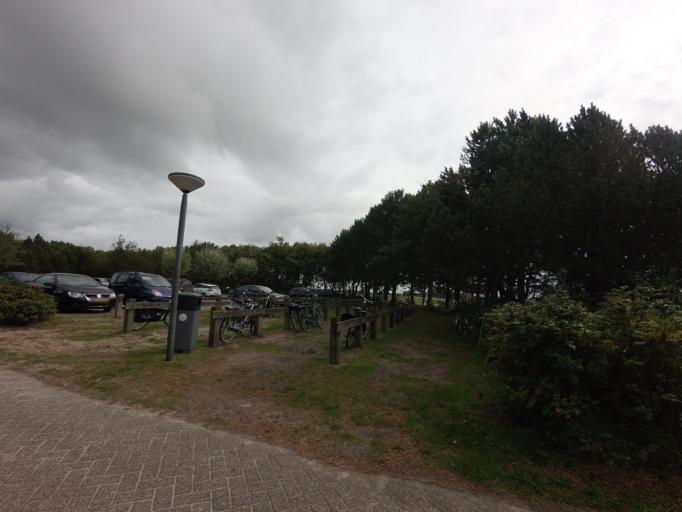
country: NL
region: Friesland
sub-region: Gemeente Ameland
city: Hollum
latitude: 53.4469
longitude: 5.6407
